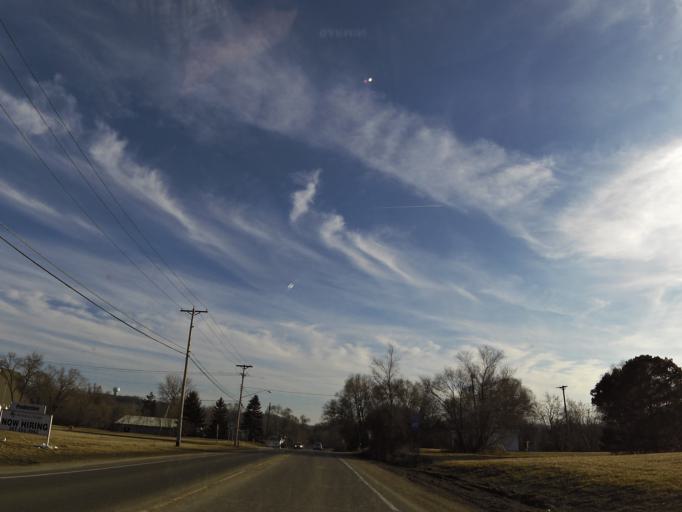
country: US
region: Minnesota
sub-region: Goodhue County
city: Cannon Falls
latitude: 44.5166
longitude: -92.9069
